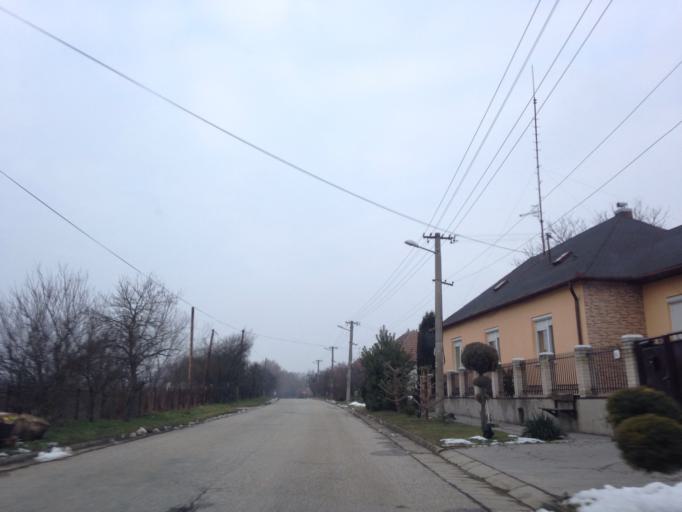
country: SK
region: Nitriansky
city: Svodin
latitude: 48.0372
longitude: 18.3727
